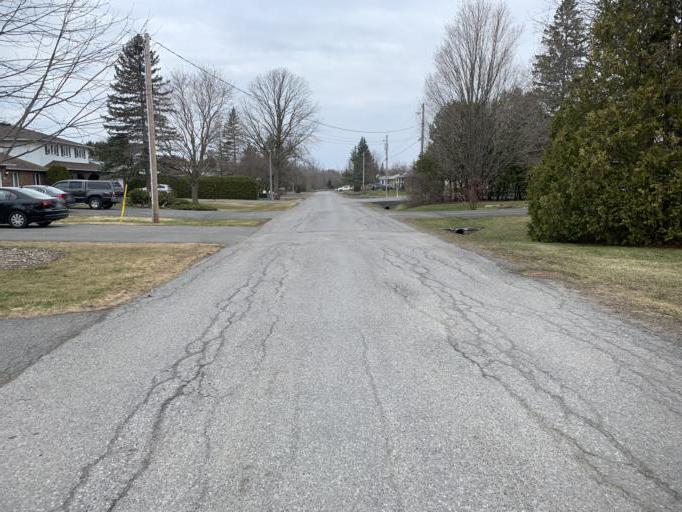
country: CA
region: Ontario
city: Bells Corners
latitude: 45.1834
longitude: -75.8304
